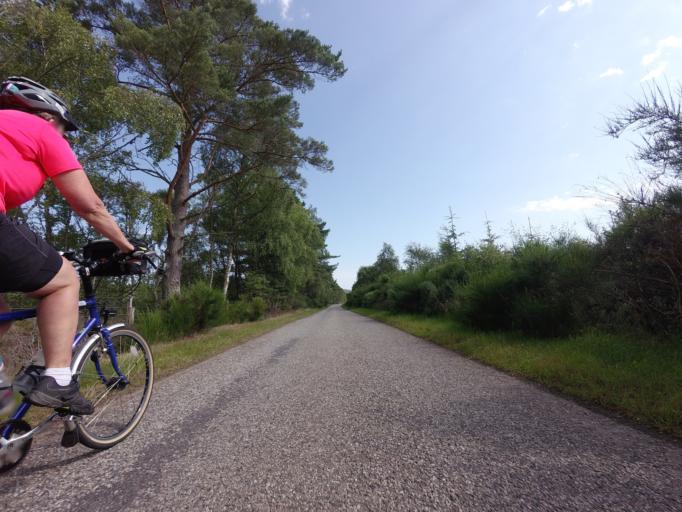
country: GB
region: Scotland
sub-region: Highland
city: Invergordon
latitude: 57.7381
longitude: -4.1857
